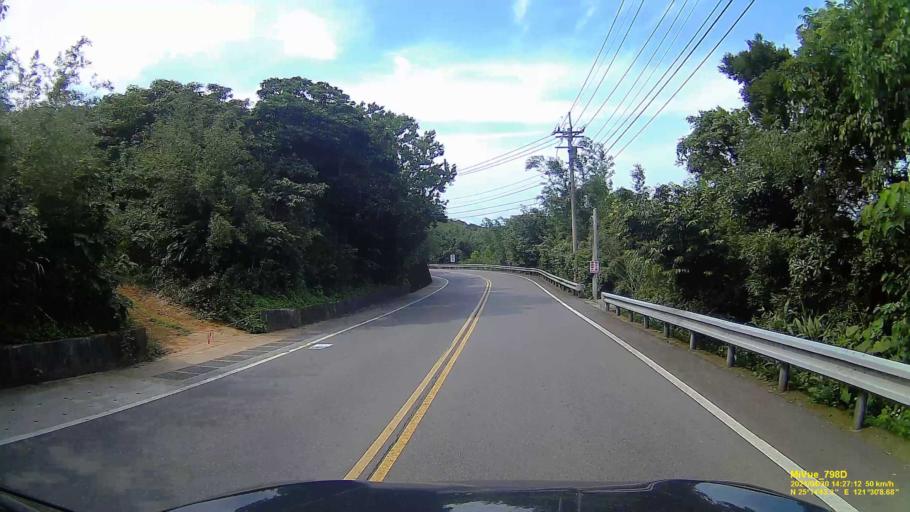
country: TW
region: Taipei
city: Taipei
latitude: 25.2456
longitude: 121.5023
